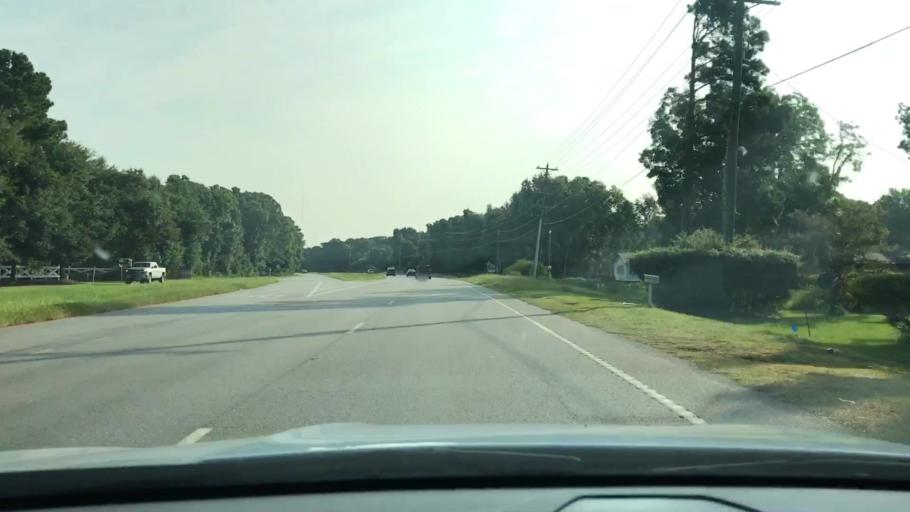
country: US
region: South Carolina
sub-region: Charleston County
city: Isle of Palms
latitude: 32.8869
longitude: -79.7447
